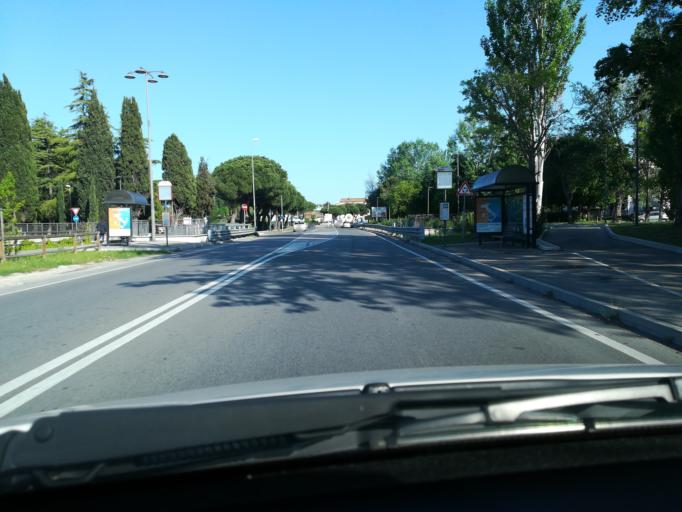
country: IT
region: Emilia-Romagna
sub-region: Provincia di Rimini
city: Riccione
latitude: 43.9995
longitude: 12.6447
